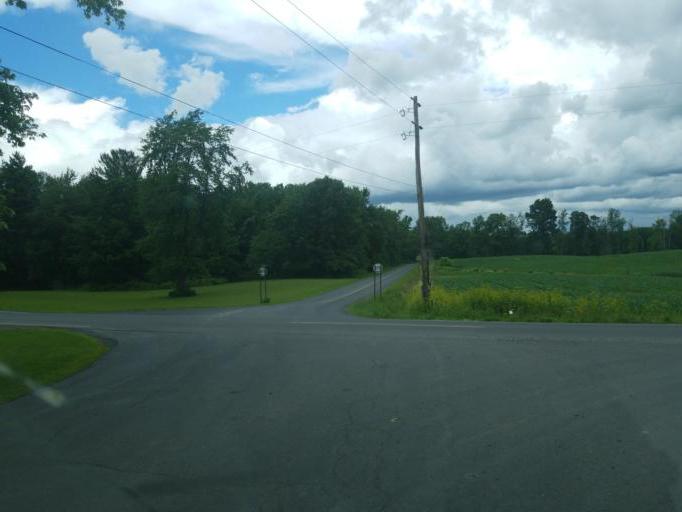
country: US
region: New York
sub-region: Wayne County
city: Lyons
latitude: 42.9953
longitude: -76.9365
